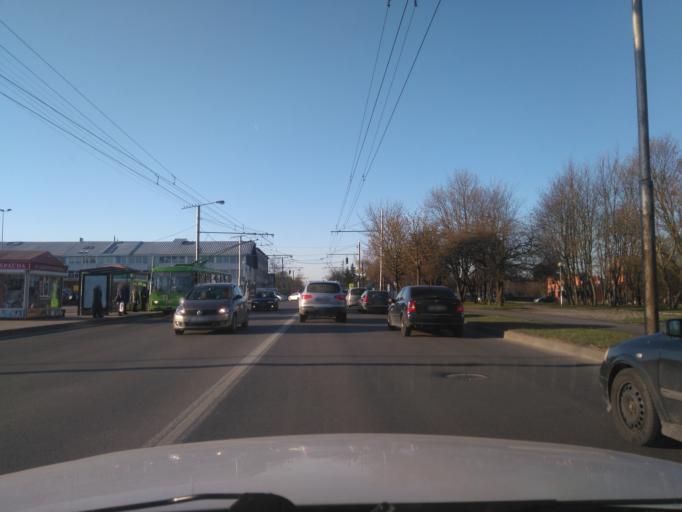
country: LT
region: Kauno apskritis
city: Dainava (Kaunas)
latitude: 54.9062
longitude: 23.9738
